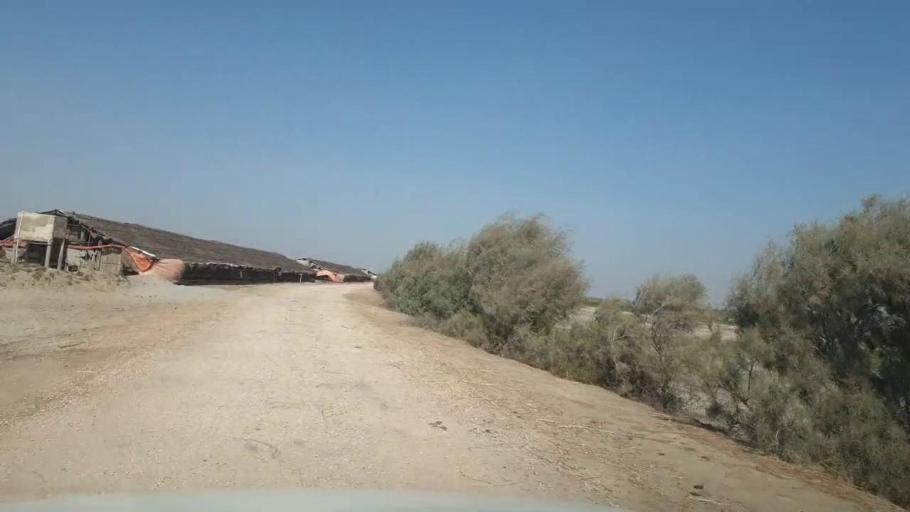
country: PK
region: Sindh
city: Chuhar Jamali
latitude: 24.3785
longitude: 67.8021
